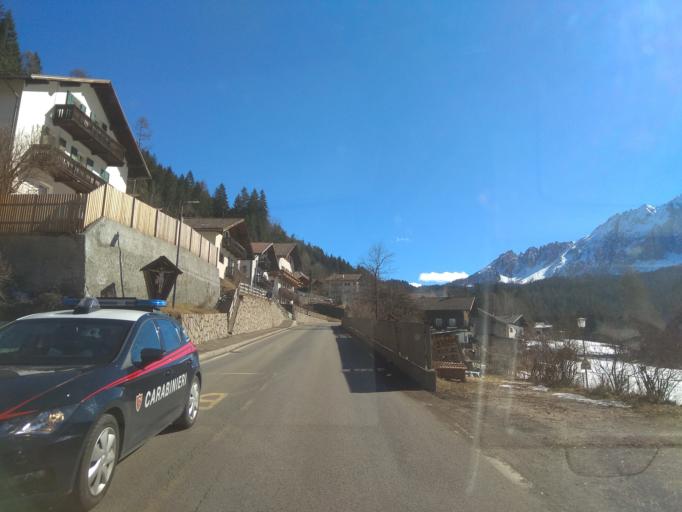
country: IT
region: Trentino-Alto Adige
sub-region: Bolzano
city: Nova Levante
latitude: 46.4254
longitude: 11.5508
